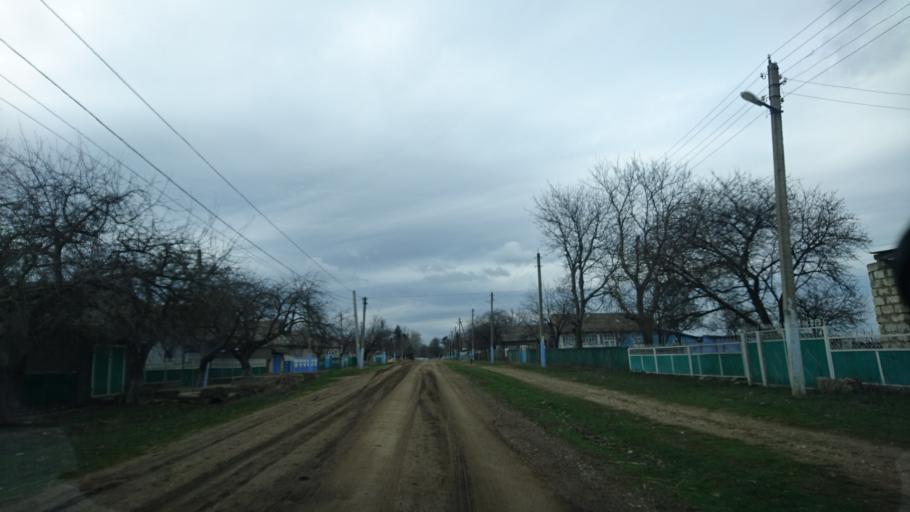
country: MD
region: Cantemir
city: Visniovca
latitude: 46.2871
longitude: 28.3767
